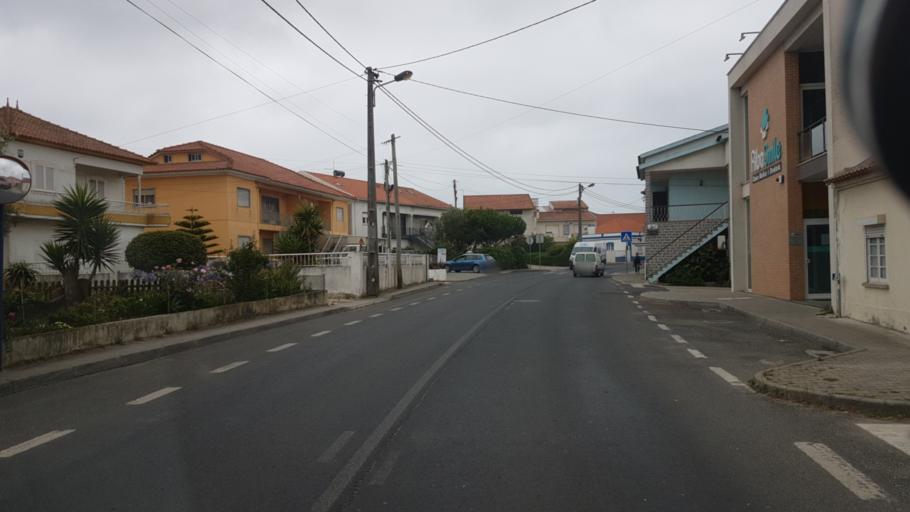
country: PT
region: Lisbon
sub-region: Lourinha
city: Lourinha
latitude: 39.2024
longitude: -9.3293
